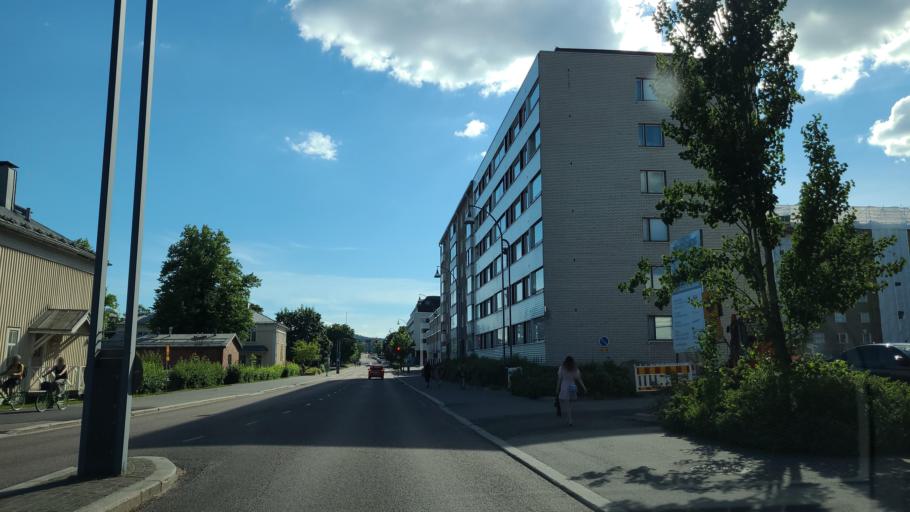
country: FI
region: Central Finland
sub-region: Jyvaeskylae
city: Jyvaeskylae
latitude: 62.2403
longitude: 25.7511
